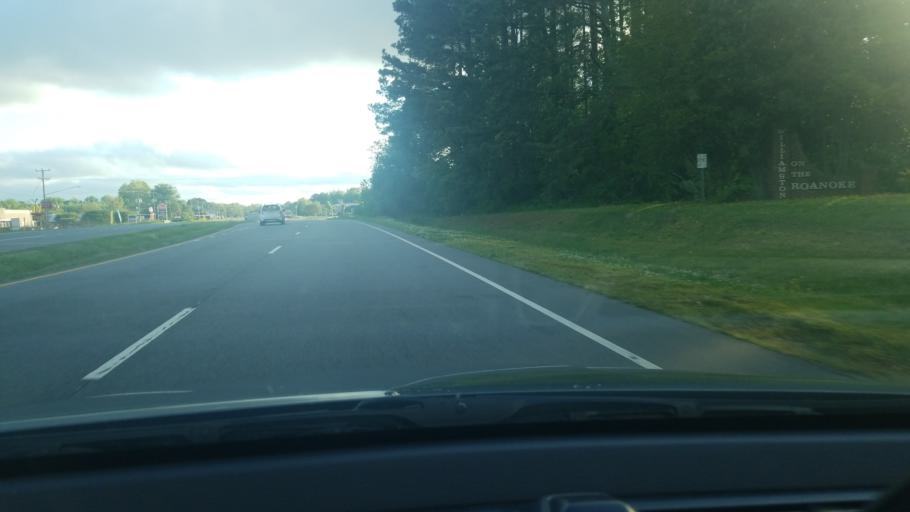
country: US
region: North Carolina
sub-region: Martin County
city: Williamston
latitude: 35.8519
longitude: -77.0469
